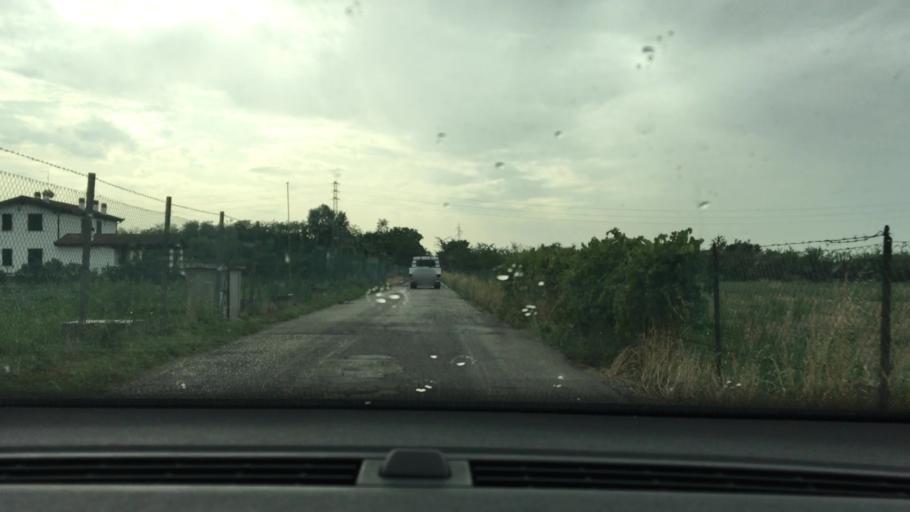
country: IT
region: Veneto
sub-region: Provincia di Verona
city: San Giovanni Lupatoto
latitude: 45.3873
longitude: 11.0153
